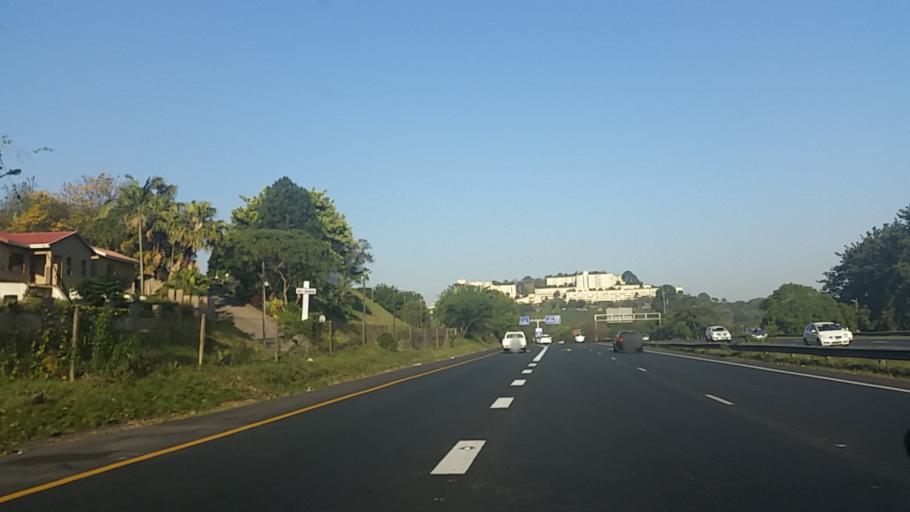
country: ZA
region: KwaZulu-Natal
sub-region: eThekwini Metropolitan Municipality
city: Berea
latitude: -29.8297
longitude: 30.8812
